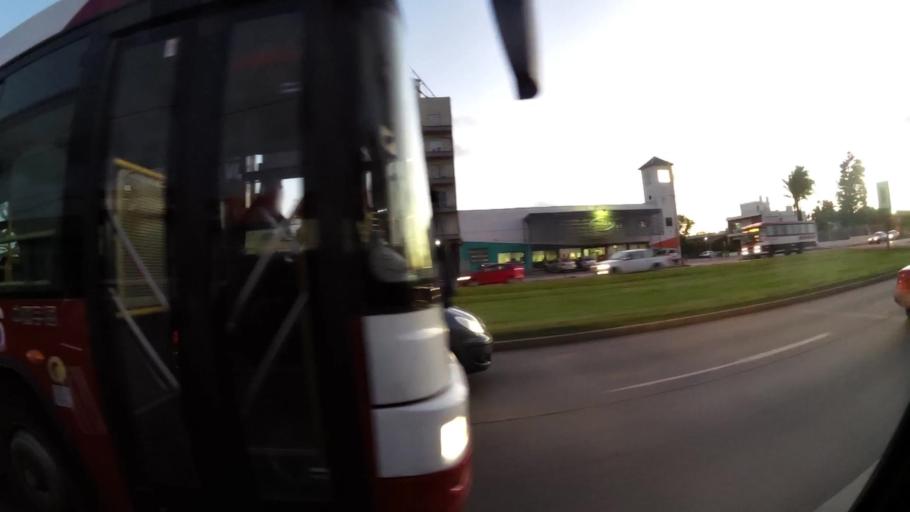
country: UY
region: Montevideo
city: Montevideo
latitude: -34.8871
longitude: -56.1197
